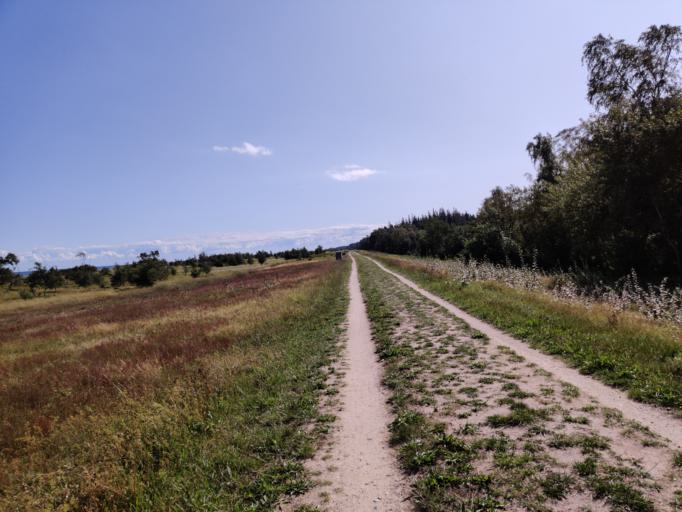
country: DK
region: Zealand
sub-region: Guldborgsund Kommune
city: Nykobing Falster
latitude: 54.6384
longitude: 11.9609
